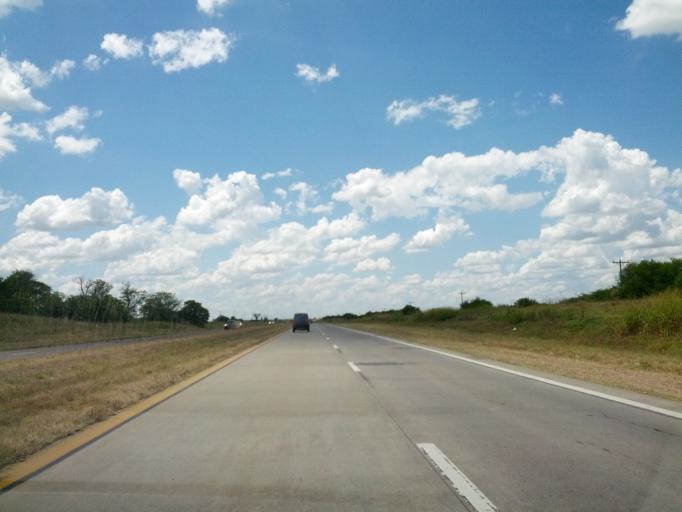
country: AR
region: Entre Rios
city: Gualeguaychu
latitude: -32.9342
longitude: -58.5730
